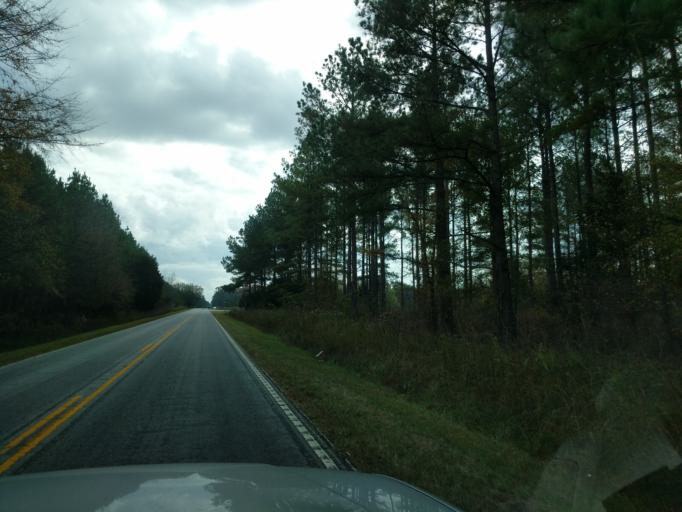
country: US
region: South Carolina
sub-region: Laurens County
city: Joanna
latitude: 34.4135
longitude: -81.8648
